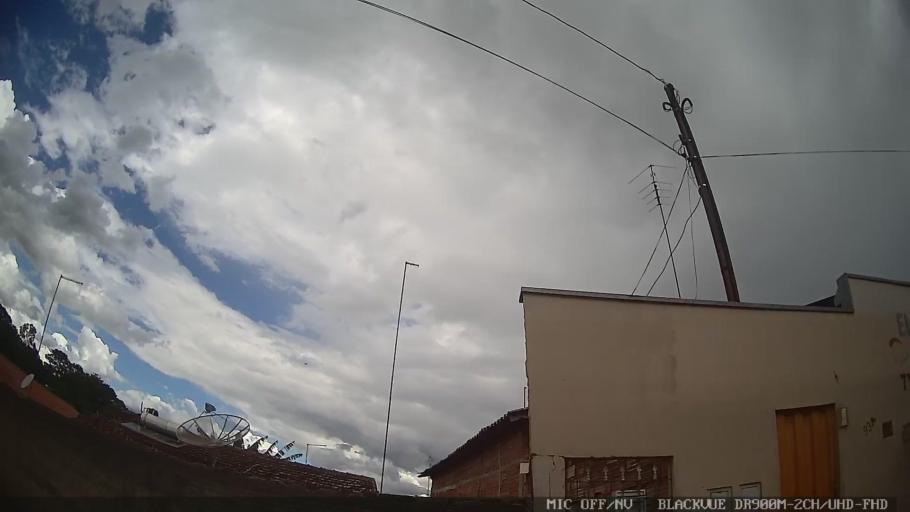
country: BR
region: Sao Paulo
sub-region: Jaguariuna
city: Jaguariuna
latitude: -22.6988
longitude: -47.0182
